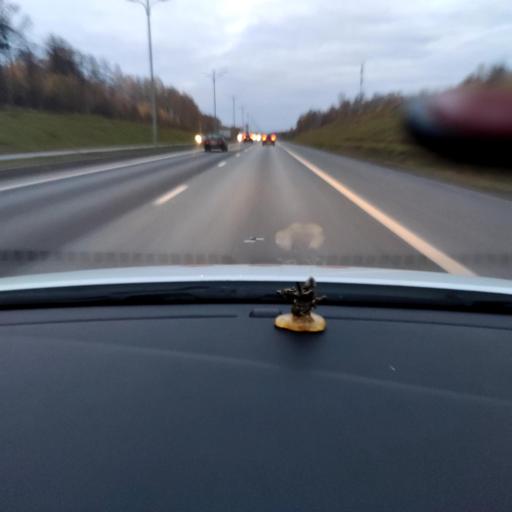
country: RU
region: Tatarstan
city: Stolbishchi
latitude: 55.7127
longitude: 49.2120
